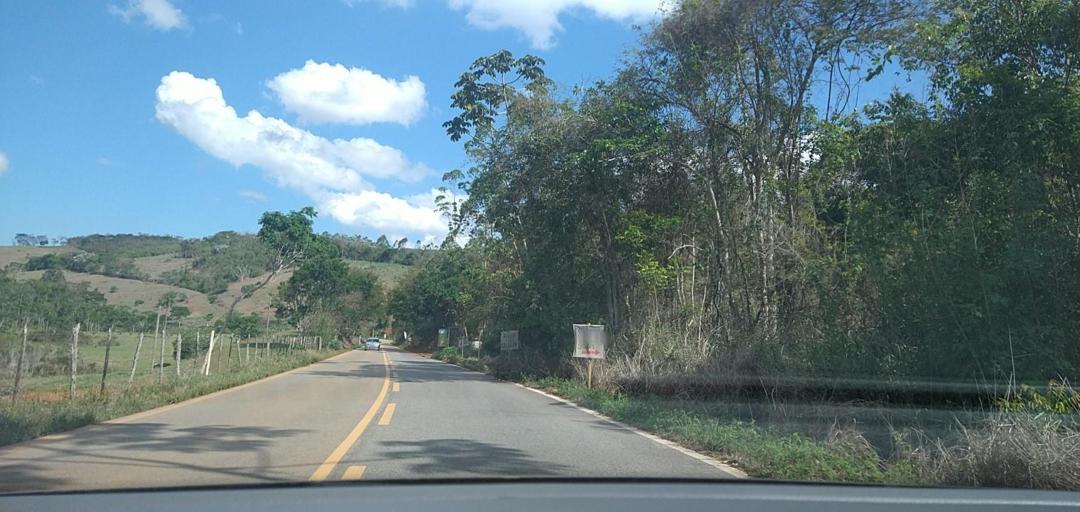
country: BR
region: Minas Gerais
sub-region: Alvinopolis
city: Alvinopolis
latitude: -20.0145
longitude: -43.0960
